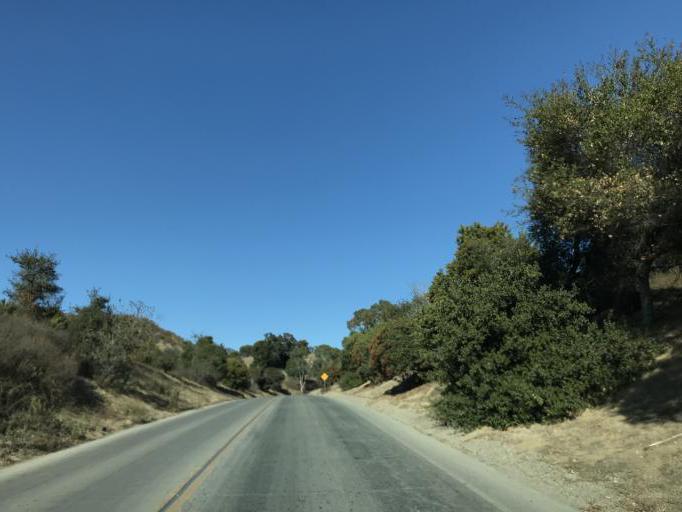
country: US
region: California
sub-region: Santa Barbara County
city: Goleta
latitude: 34.4446
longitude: -119.7757
